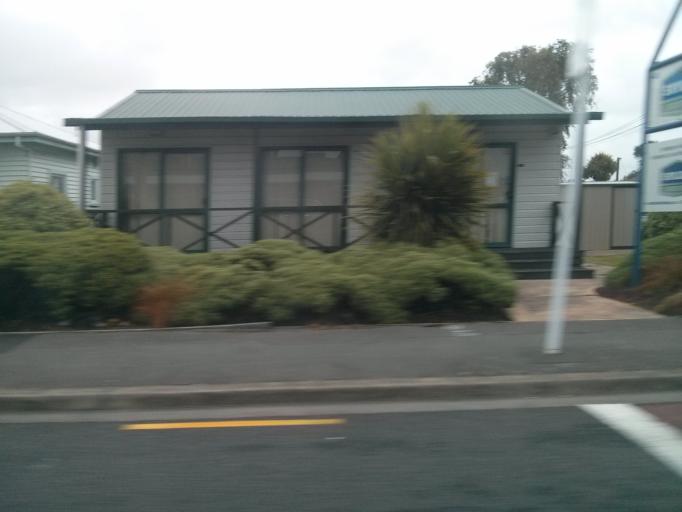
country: NZ
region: Canterbury
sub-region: Christchurch City
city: Christchurch
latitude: -43.4948
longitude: 172.6094
